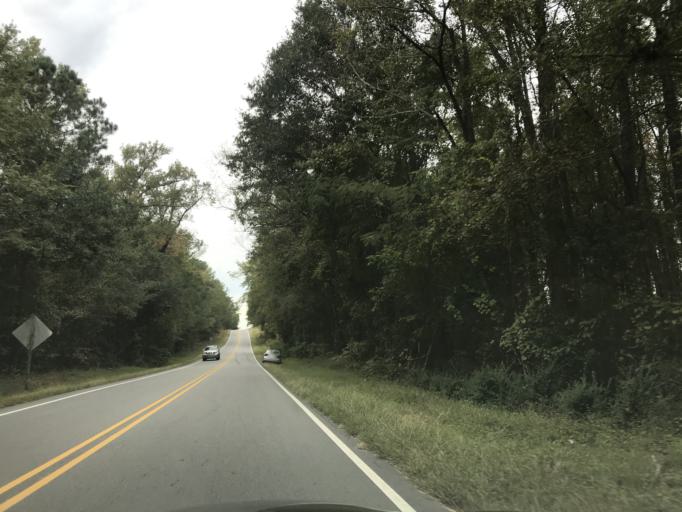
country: US
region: North Carolina
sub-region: Wake County
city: Knightdale
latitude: 35.8113
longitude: -78.4934
